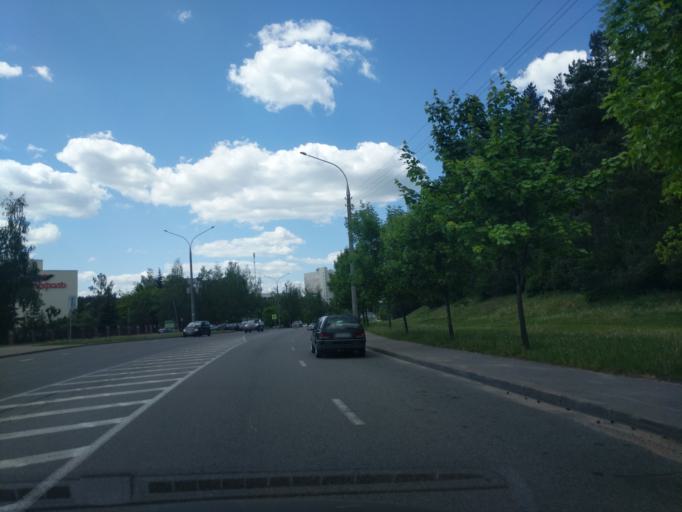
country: BY
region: Minsk
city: Borovlyany
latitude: 53.9236
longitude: 27.6731
